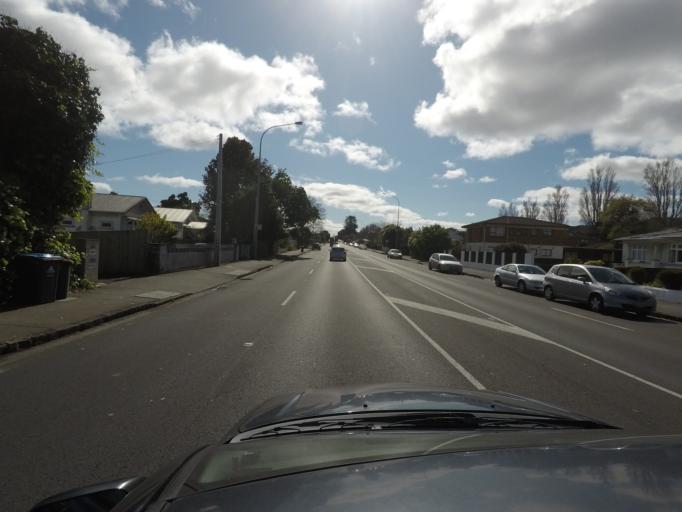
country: NZ
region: Auckland
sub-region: Auckland
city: Rosebank
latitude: -36.8920
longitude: 174.7074
